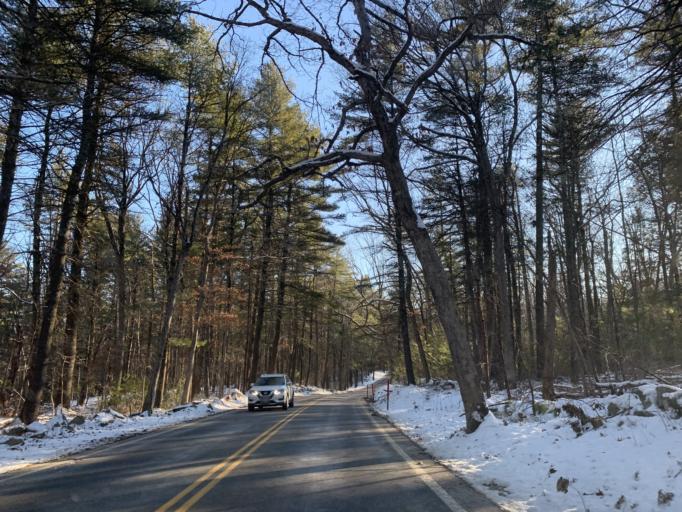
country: US
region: Massachusetts
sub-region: Norfolk County
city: Sharon
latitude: 42.1150
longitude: -71.2089
